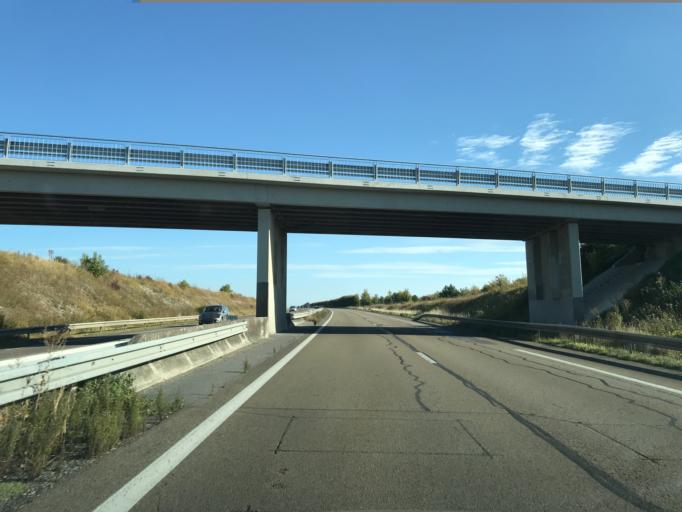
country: FR
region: Champagne-Ardenne
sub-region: Departement de la Marne
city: Verzy
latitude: 49.1338
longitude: 4.2218
